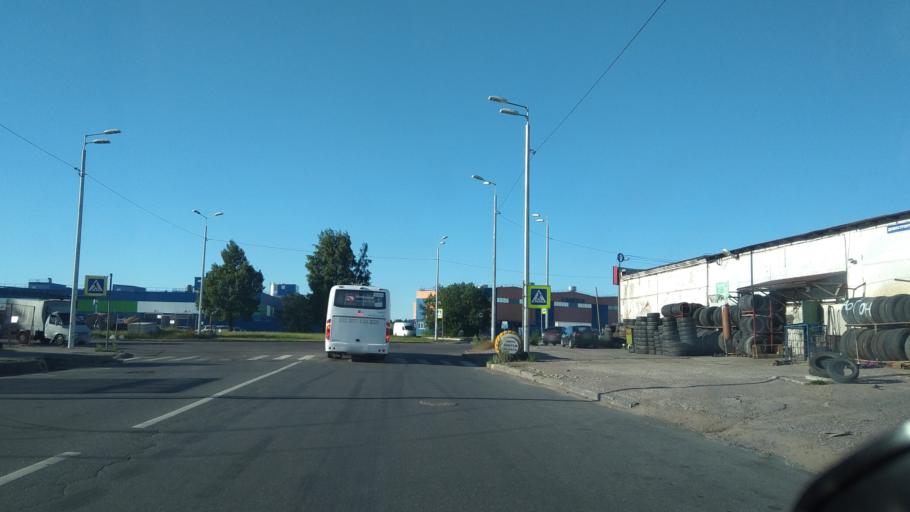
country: RU
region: Leningrad
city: Bugry
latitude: 60.0732
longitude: 30.3747
